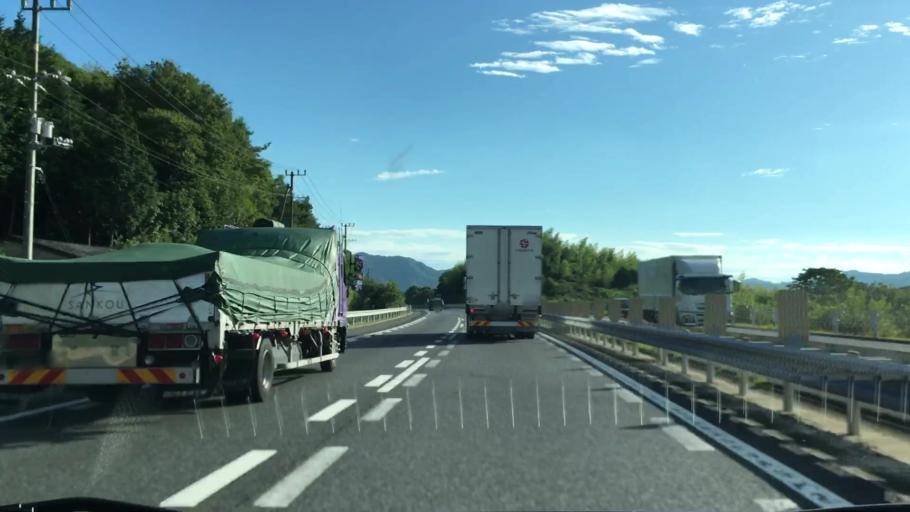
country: JP
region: Yamaguchi
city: Yanai
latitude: 34.0972
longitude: 132.0990
